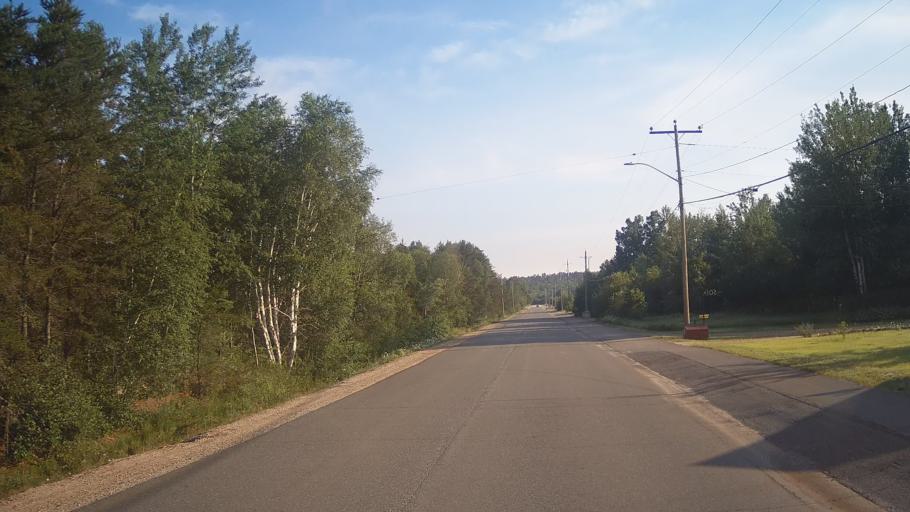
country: CA
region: Ontario
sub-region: Rainy River District
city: Atikokan
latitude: 49.4116
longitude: -91.6659
